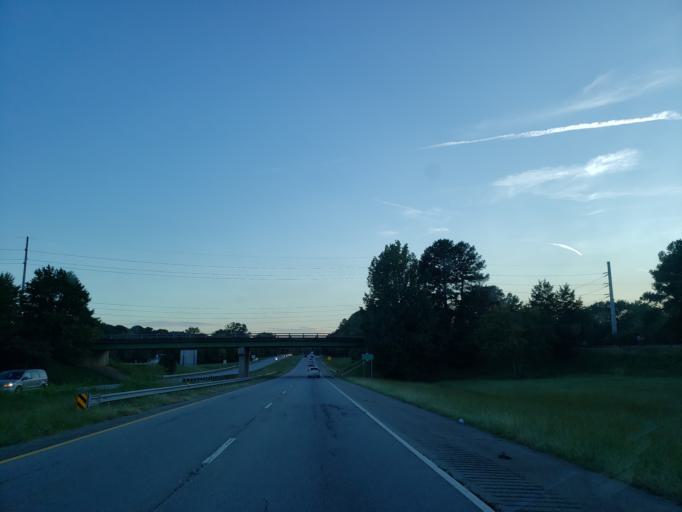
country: US
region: Georgia
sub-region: Floyd County
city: Lindale
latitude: 34.2205
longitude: -85.1739
